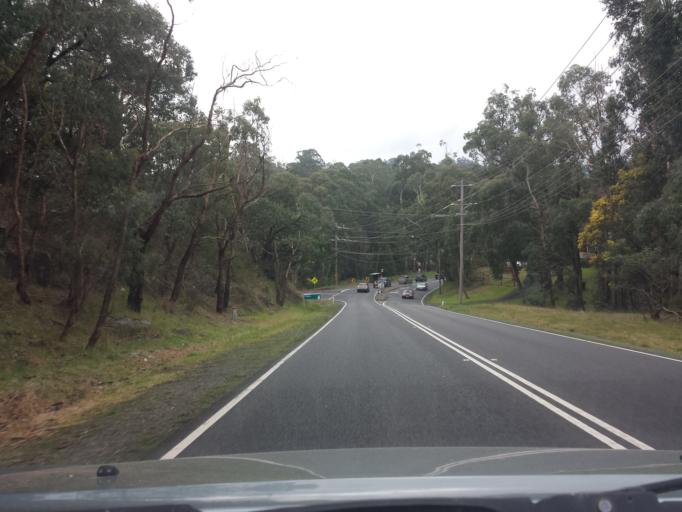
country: AU
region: Victoria
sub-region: Yarra Ranges
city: Belgrave Heights
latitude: -37.9229
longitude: 145.3570
